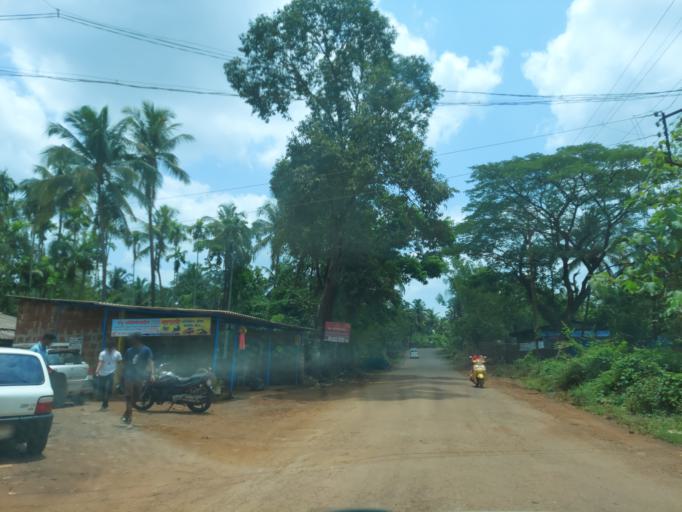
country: IN
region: Maharashtra
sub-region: Sindhudurg
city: Savantvadi
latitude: 15.8214
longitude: 73.8722
